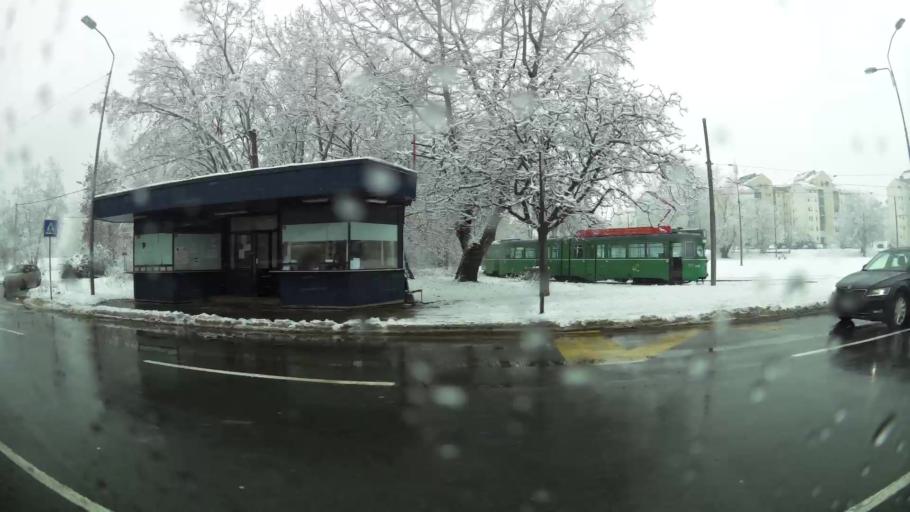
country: RS
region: Central Serbia
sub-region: Belgrade
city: Cukarica
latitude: 44.7929
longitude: 20.3753
